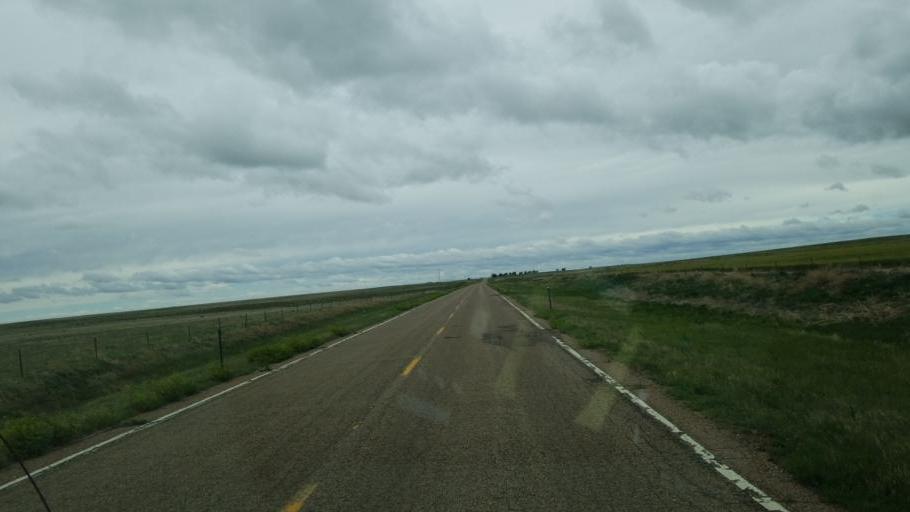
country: US
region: Colorado
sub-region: Lincoln County
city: Hugo
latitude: 38.8518
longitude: -103.6783
